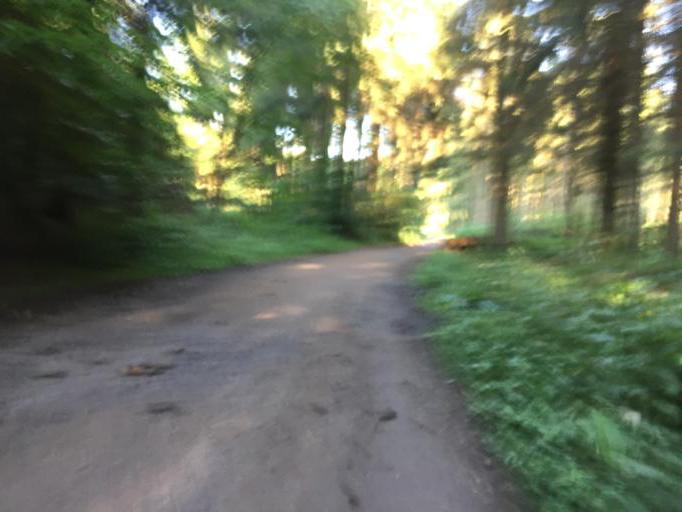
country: DE
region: Rheinland-Pfalz
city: Berod bei Wallmerod
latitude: 50.4954
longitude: 7.9231
